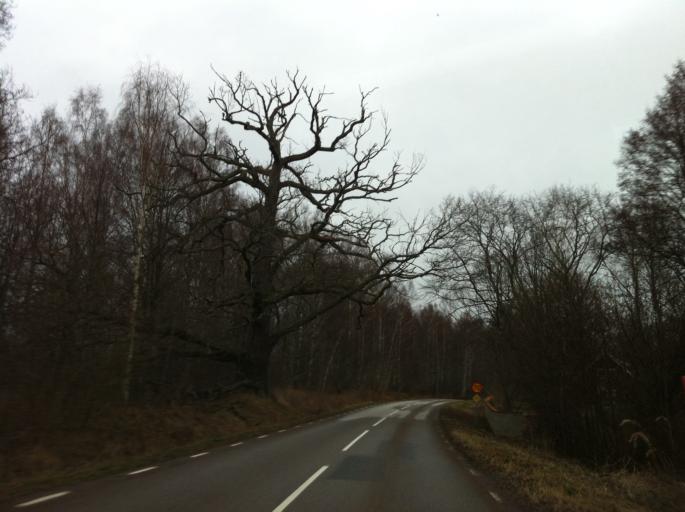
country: SE
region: Kalmar
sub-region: Vasterviks Kommun
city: Vaestervik
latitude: 57.8223
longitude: 16.5698
